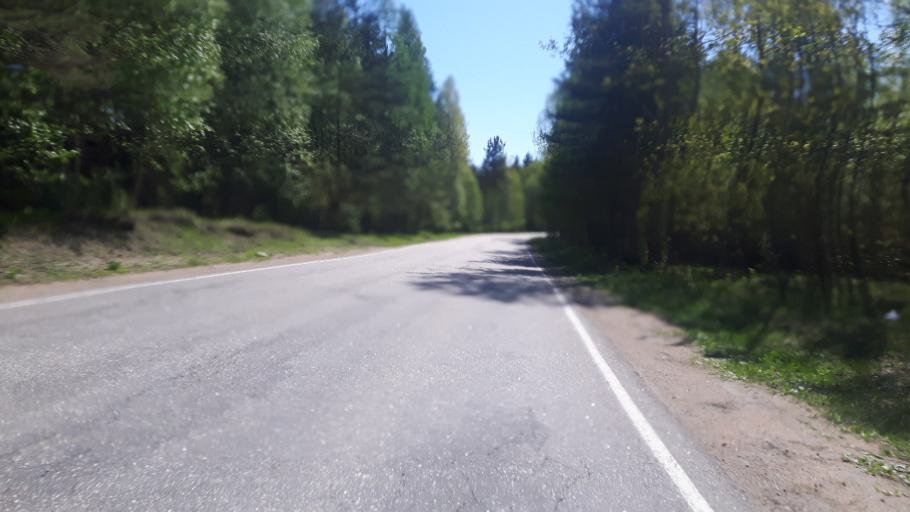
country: RU
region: Leningrad
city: Glebychevo
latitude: 60.3422
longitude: 28.8228
